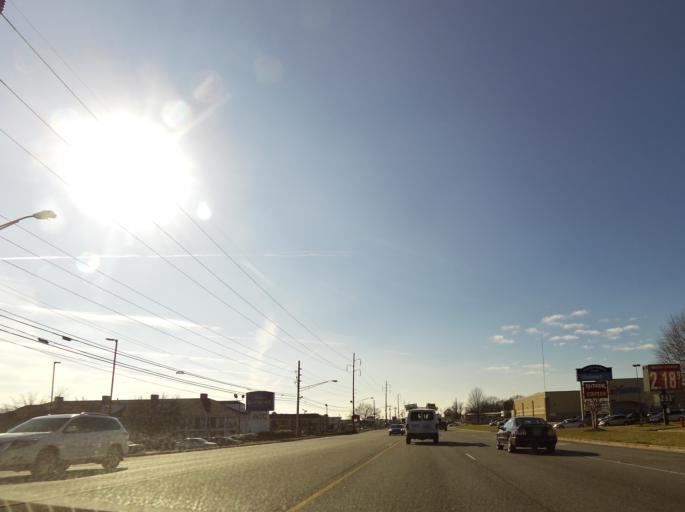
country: US
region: Georgia
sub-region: Houston County
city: Centerville
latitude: 32.6184
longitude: -83.6732
